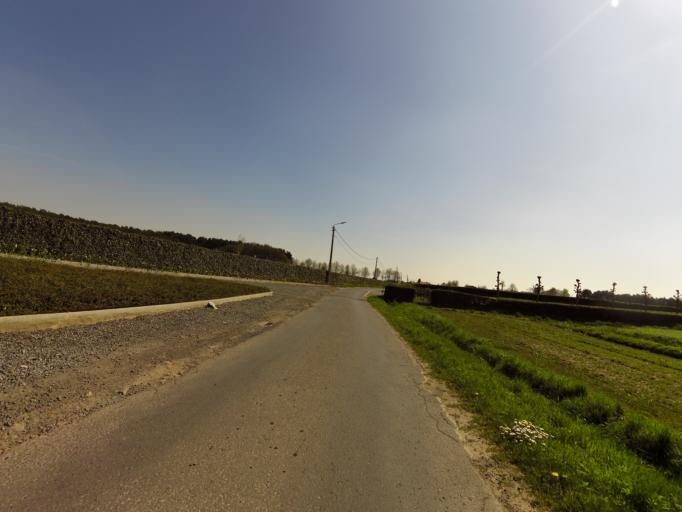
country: BE
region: Flanders
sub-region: Provincie West-Vlaanderen
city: Kortemark
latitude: 51.0590
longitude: 3.0198
